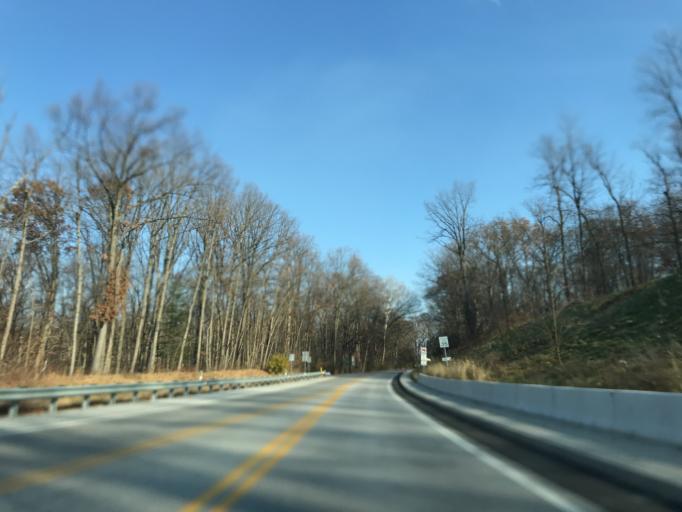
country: US
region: Pennsylvania
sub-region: York County
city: Loganville
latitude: 39.8662
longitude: -76.6962
